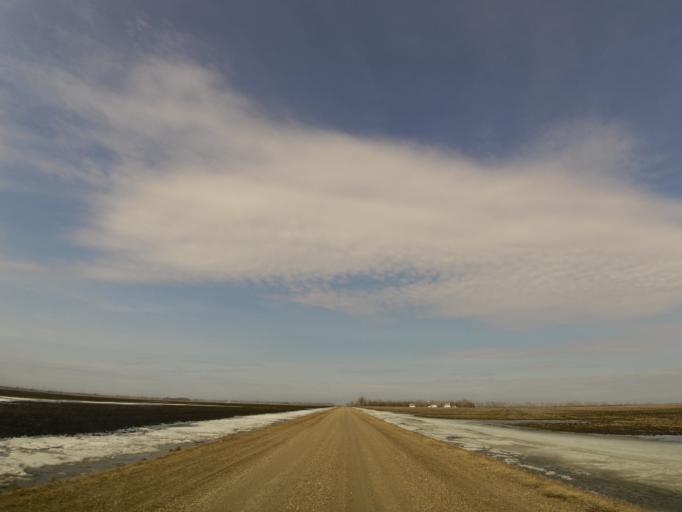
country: US
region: North Dakota
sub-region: Walsh County
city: Grafton
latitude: 48.4193
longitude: -97.2557
